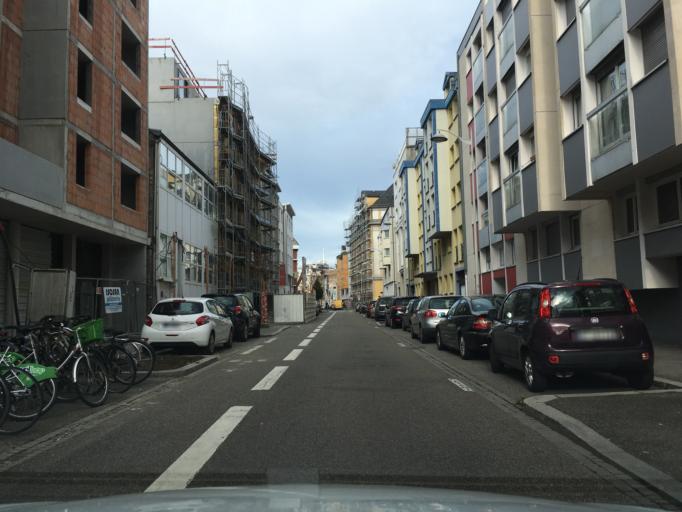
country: FR
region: Alsace
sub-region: Departement du Bas-Rhin
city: Strasbourg
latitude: 48.5892
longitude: 7.7391
